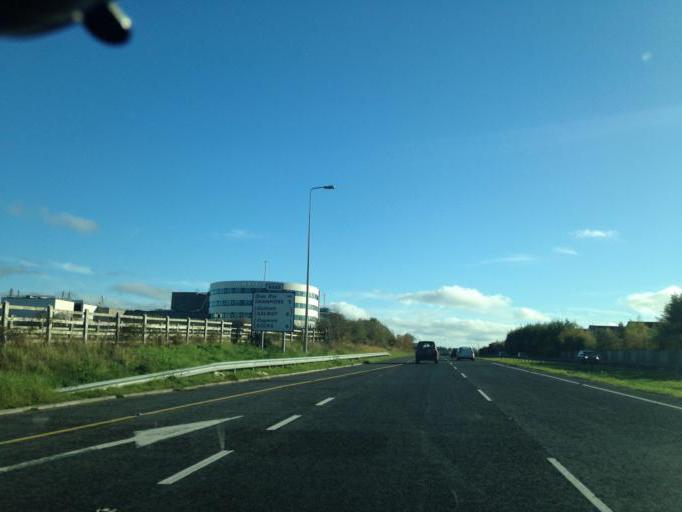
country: IE
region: Connaught
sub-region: County Galway
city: Oranmore
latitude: 53.2836
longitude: -8.9773
